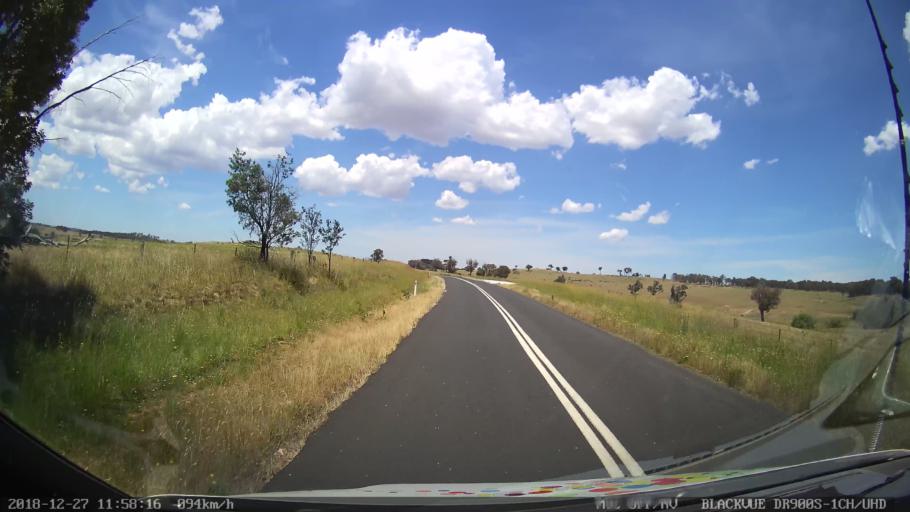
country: AU
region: New South Wales
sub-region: Blayney
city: Blayney
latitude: -33.7217
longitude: 149.3847
